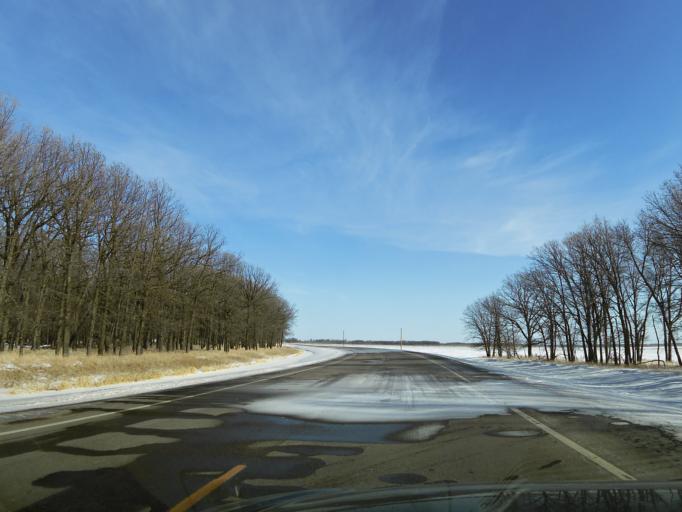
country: US
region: North Dakota
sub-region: Walsh County
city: Grafton
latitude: 48.4140
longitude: -97.1282
